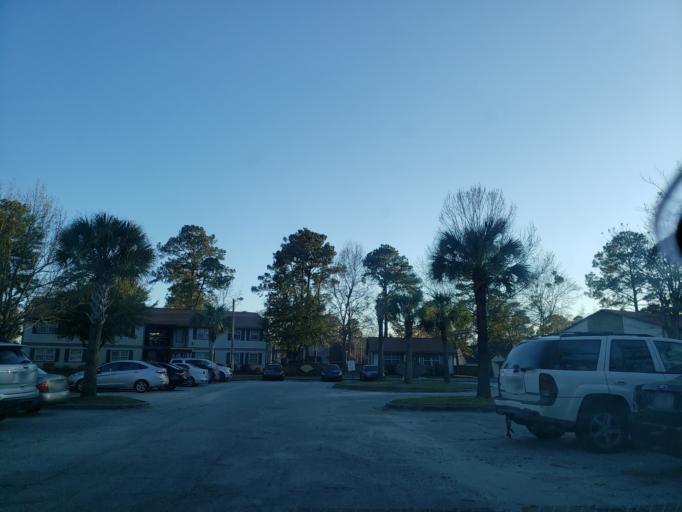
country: US
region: Georgia
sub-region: Chatham County
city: Montgomery
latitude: 32.0004
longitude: -81.1377
